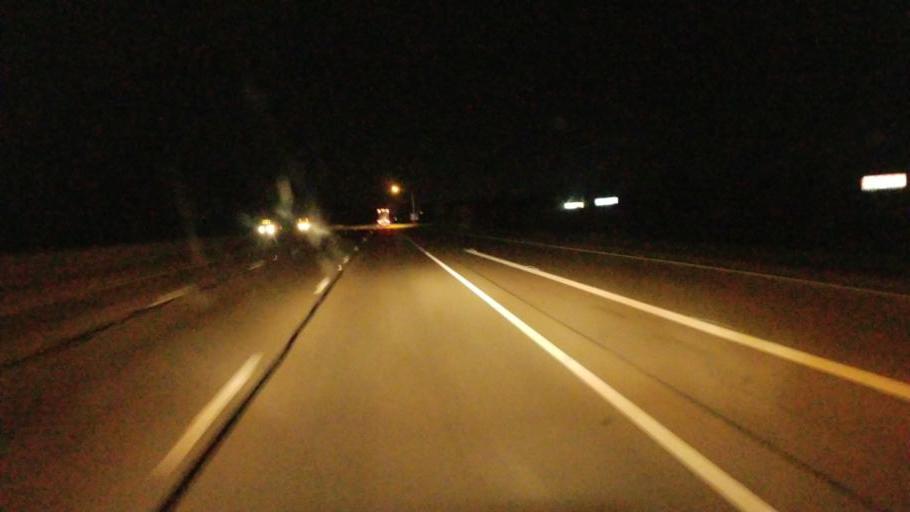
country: US
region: Ohio
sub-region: Clark County
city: Crystal Lakes
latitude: 39.8649
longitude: -84.0024
